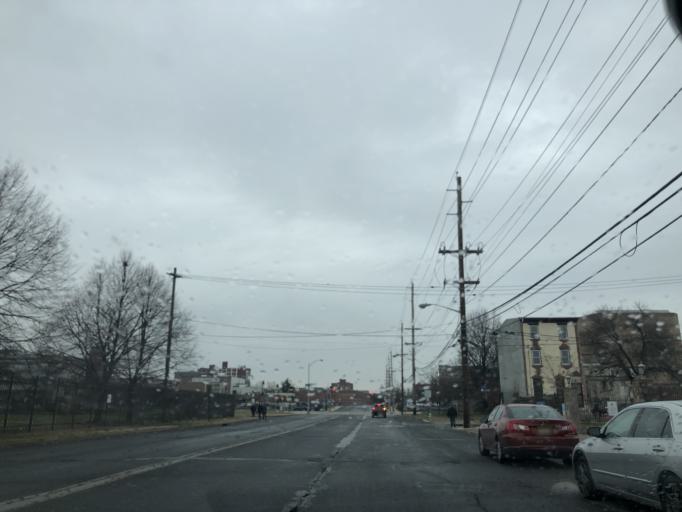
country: US
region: New Jersey
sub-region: Camden County
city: Camden
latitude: 39.9413
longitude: -75.1248
